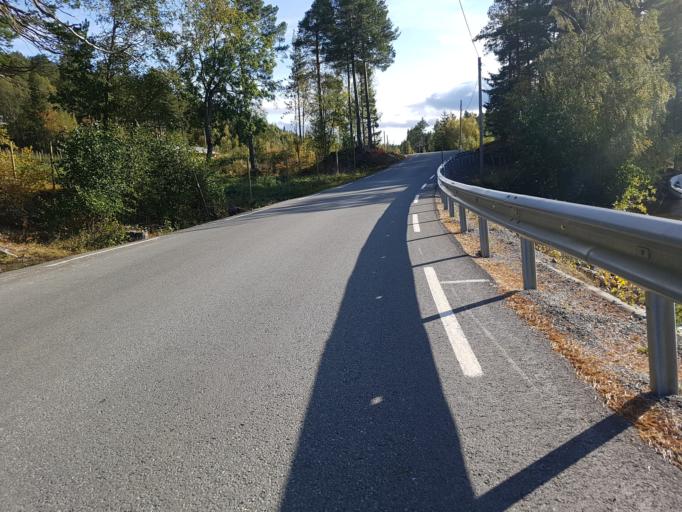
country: NO
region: Sor-Trondelag
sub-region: Malvik
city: Malvik
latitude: 63.3740
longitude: 10.6114
